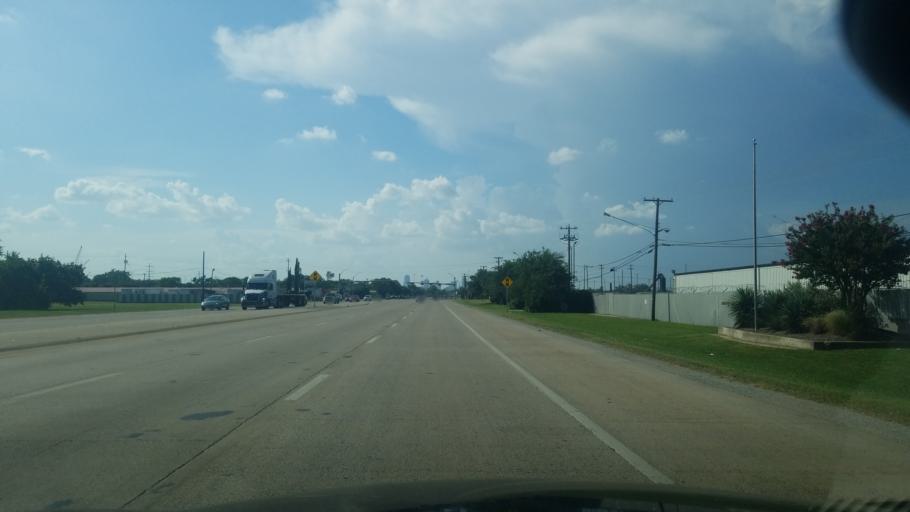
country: US
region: Texas
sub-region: Dallas County
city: Hutchins
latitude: 32.7135
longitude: -96.7537
